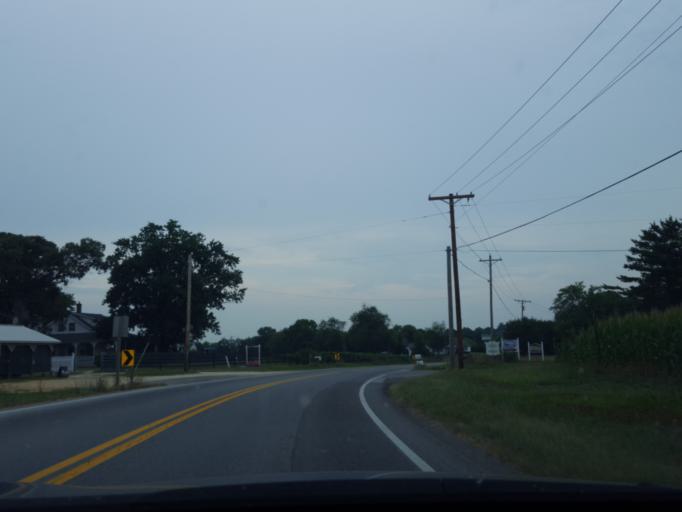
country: US
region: Maryland
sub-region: Saint Mary's County
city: Charlotte Hall
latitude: 38.4477
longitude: -76.7900
